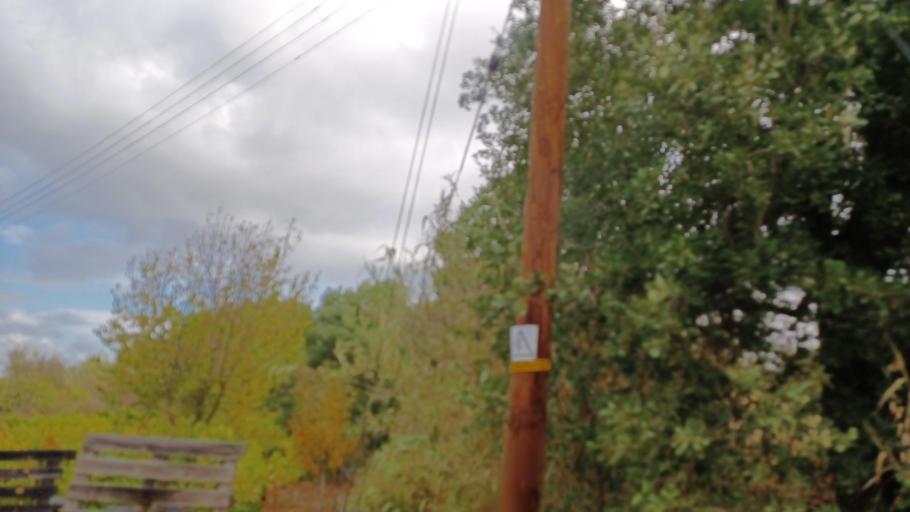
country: CY
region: Pafos
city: Polis
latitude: 35.0072
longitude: 32.4962
